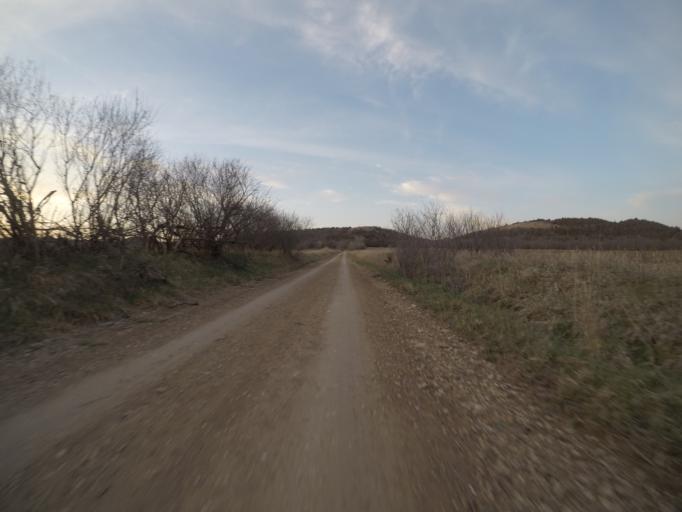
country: US
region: Kansas
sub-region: Riley County
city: Ogden
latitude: 39.1637
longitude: -96.6678
